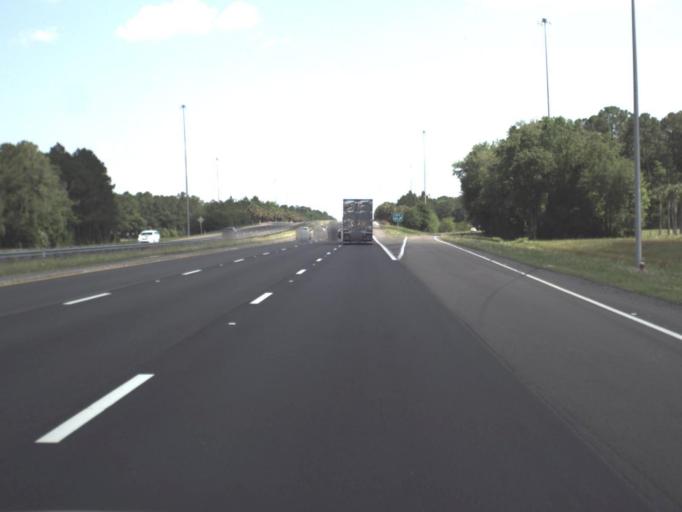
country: US
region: Florida
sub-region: Nassau County
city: Yulee
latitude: 30.5131
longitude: -81.6344
